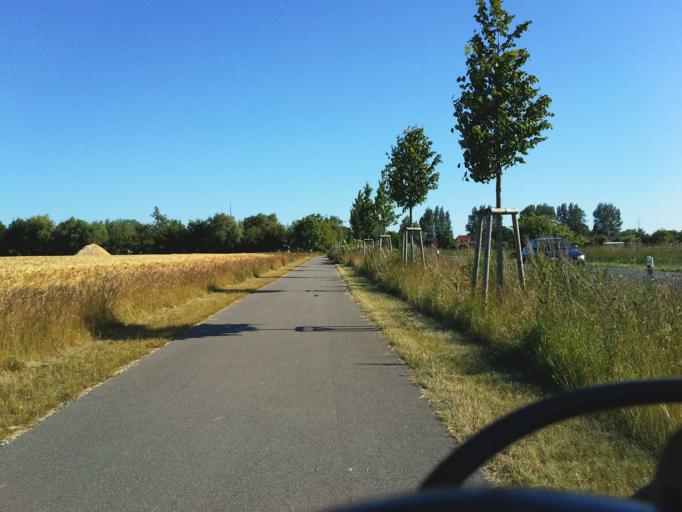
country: DE
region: Mecklenburg-Vorpommern
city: Nienhagen
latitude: 54.1529
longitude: 12.1757
